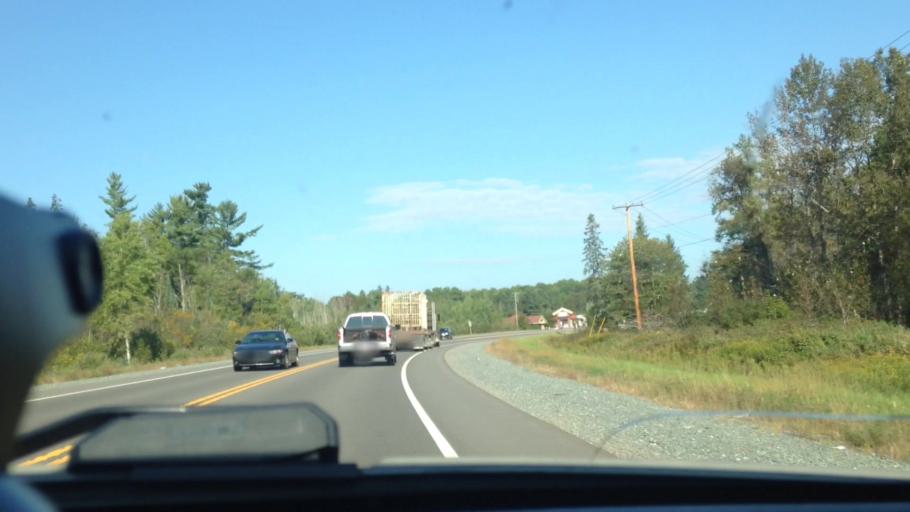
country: US
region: Michigan
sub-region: Dickinson County
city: Iron Mountain
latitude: 45.8669
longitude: -88.0797
